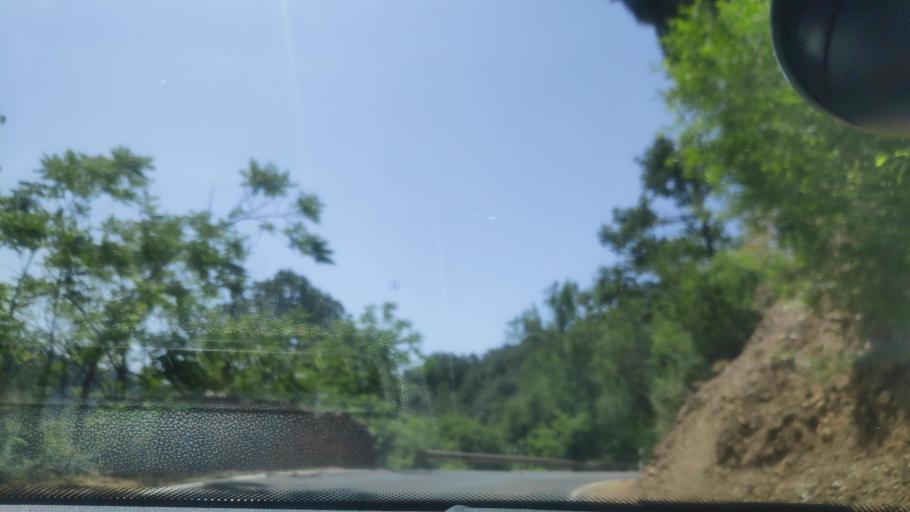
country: ES
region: Andalusia
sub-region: Provincia de Granada
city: Trevelez
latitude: 36.9821
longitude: -3.2797
